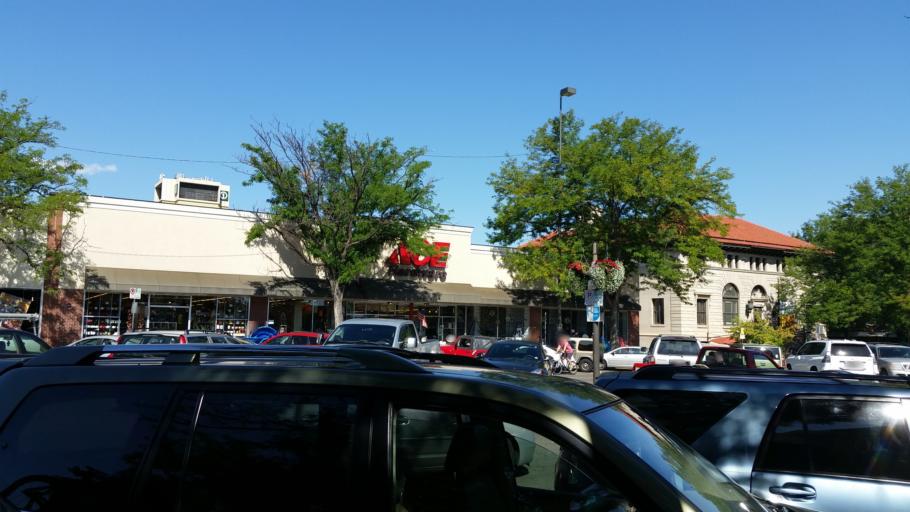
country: US
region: Colorado
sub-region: Larimer County
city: Fort Collins
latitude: 40.5847
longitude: -105.0769
